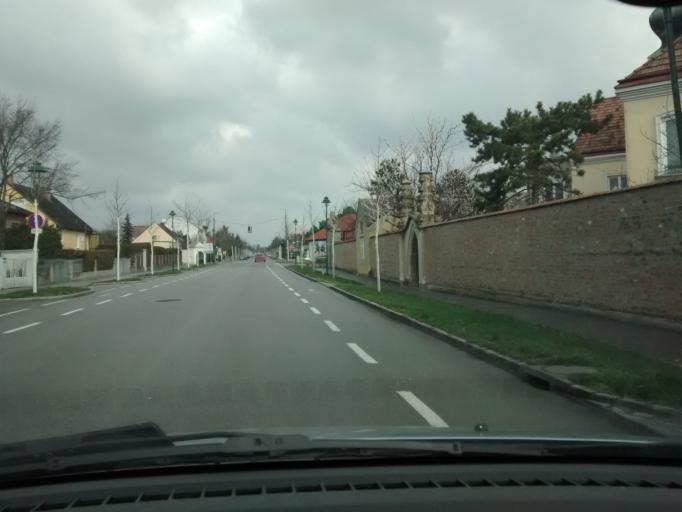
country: AT
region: Lower Austria
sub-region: Politischer Bezirk Modling
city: Laxenburg
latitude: 48.0707
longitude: 16.3550
